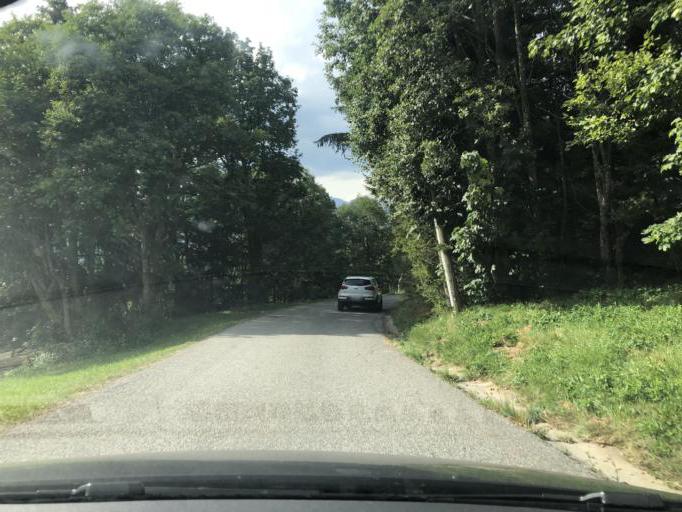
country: FR
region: Rhone-Alpes
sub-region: Departement de la Haute-Savoie
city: Megeve
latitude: 45.8395
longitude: 6.6433
